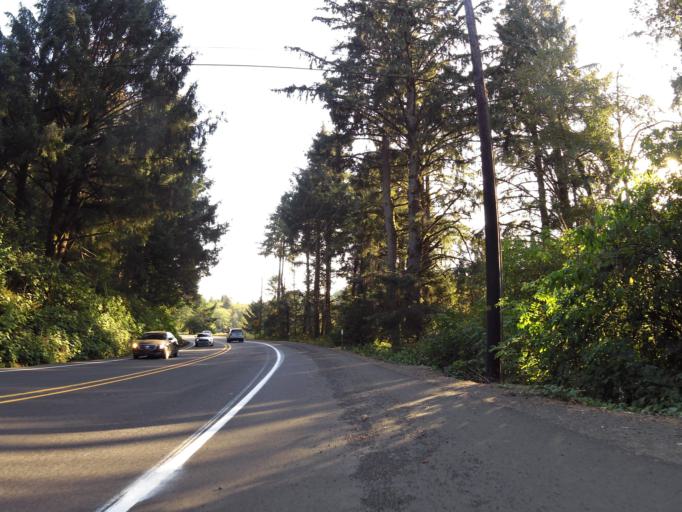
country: US
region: Oregon
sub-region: Lincoln County
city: Lincoln City
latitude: 45.0137
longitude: -123.9788
